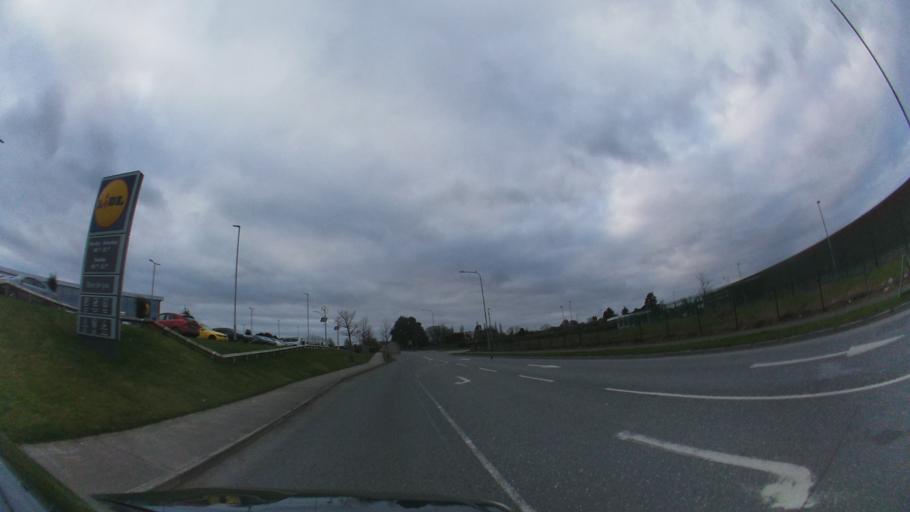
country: IE
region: Leinster
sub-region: Lu
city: Drogheda
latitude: 53.7075
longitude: -6.3704
